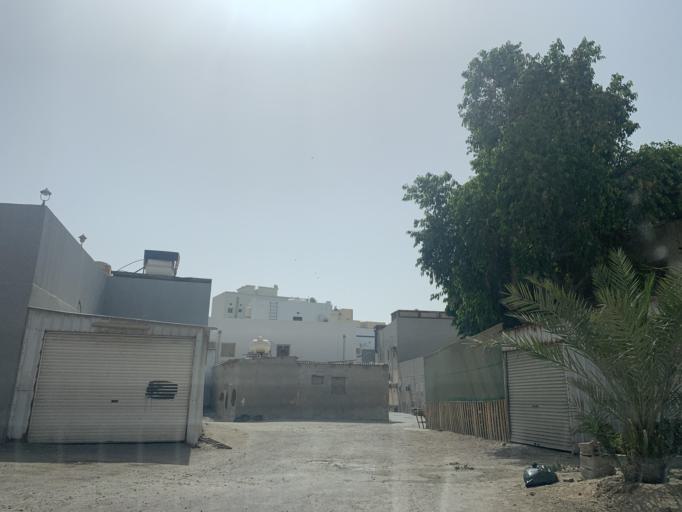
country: BH
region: Northern
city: Sitrah
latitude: 26.1619
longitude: 50.6079
